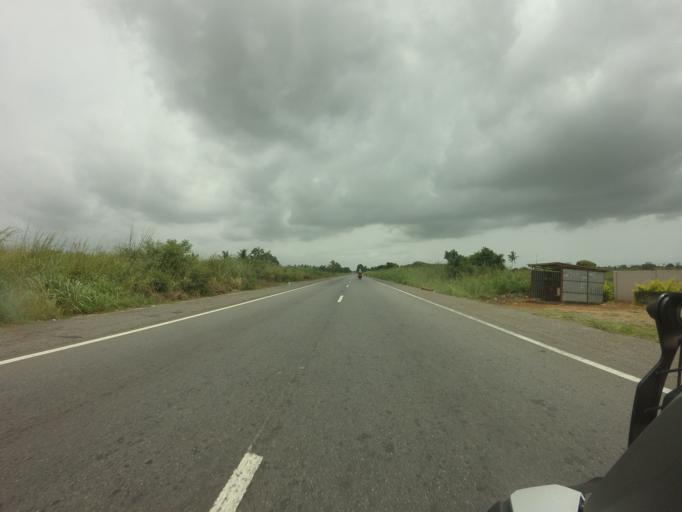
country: GH
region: Volta
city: Keta
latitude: 6.0657
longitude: 0.8844
